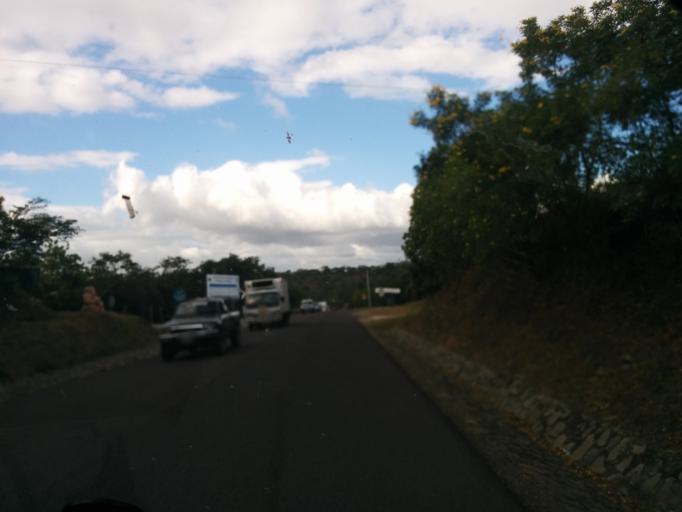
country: NI
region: Esteli
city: Esteli
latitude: 13.1803
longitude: -86.3693
